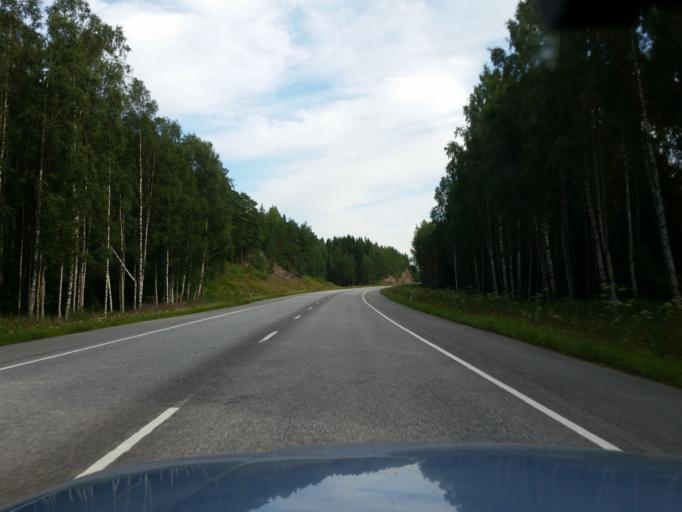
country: FI
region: Uusimaa
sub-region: Raaseporin
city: Karis
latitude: 60.0740
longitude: 23.7701
